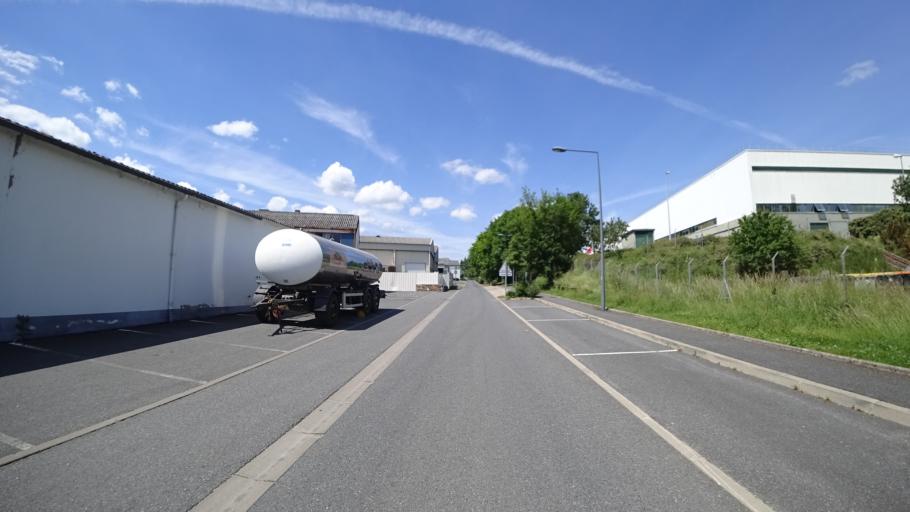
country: FR
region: Midi-Pyrenees
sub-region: Departement de l'Aveyron
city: Le Monastere
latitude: 44.3594
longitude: 2.5984
